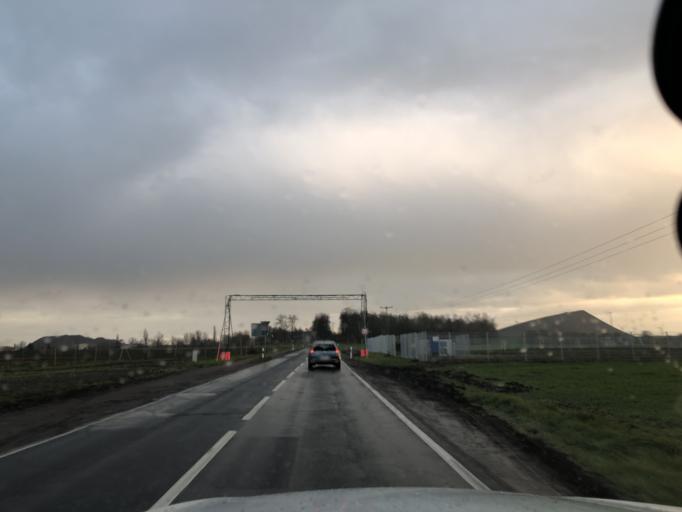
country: DE
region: Saxony-Anhalt
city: Langenbogen
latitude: 51.4776
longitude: 11.7803
